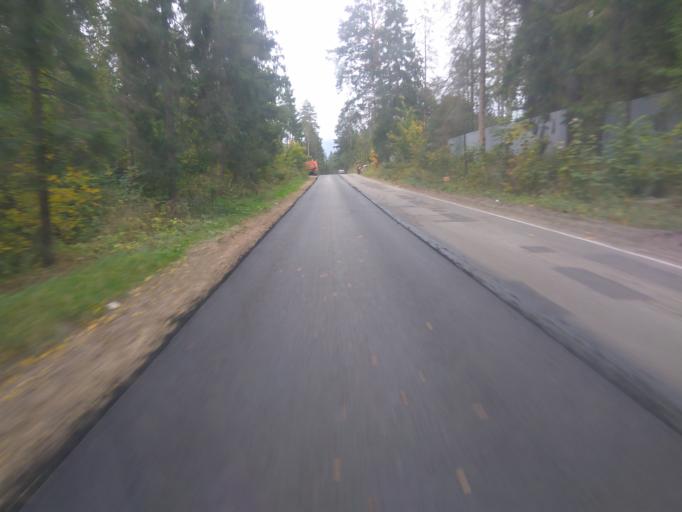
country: RU
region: Moskovskaya
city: Chupryakovo
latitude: 55.6091
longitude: 36.6089
